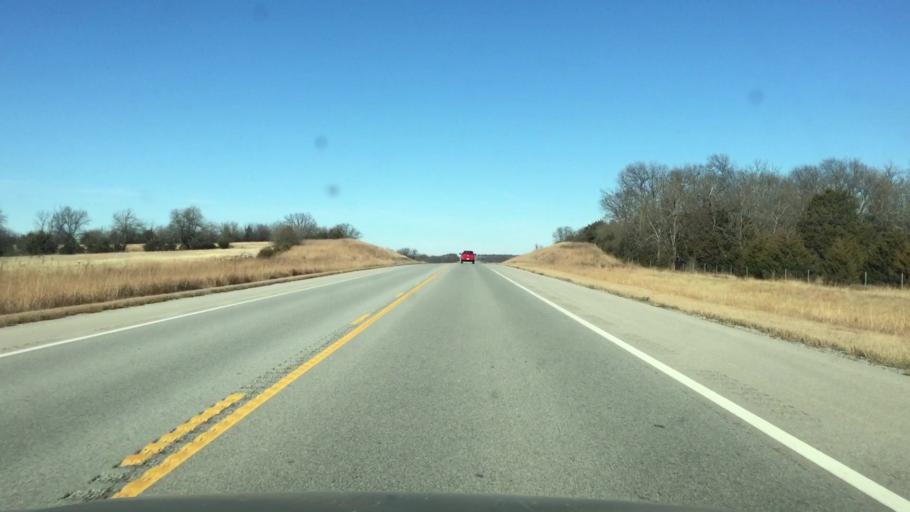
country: US
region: Kansas
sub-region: Allen County
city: Iola
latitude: 37.9699
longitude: -95.3811
